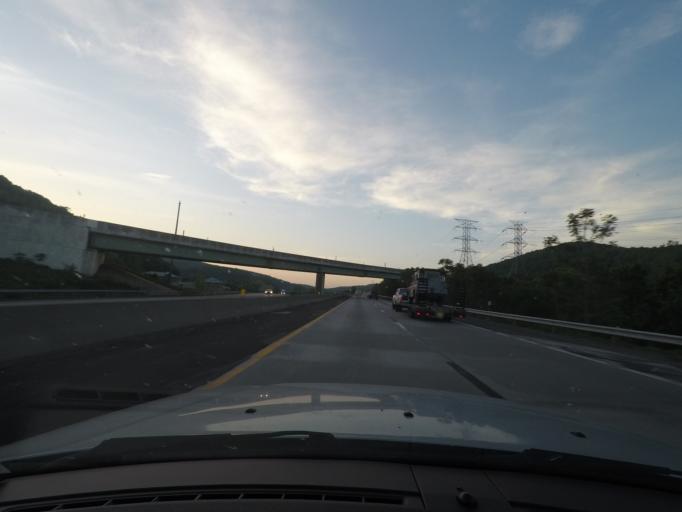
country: US
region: New York
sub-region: Rockland County
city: Suffern
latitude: 41.1172
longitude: -74.1614
